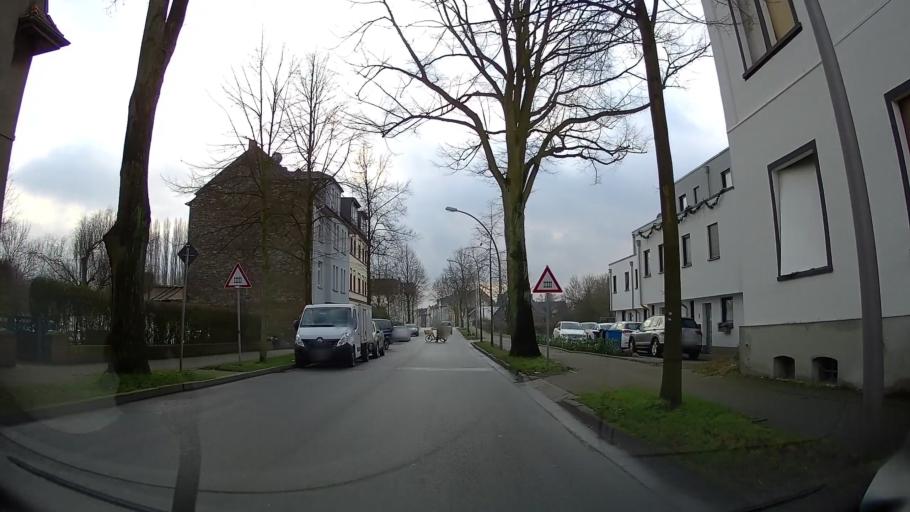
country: DE
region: North Rhine-Westphalia
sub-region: Regierungsbezirk Munster
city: Gladbeck
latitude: 51.5402
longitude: 7.0082
